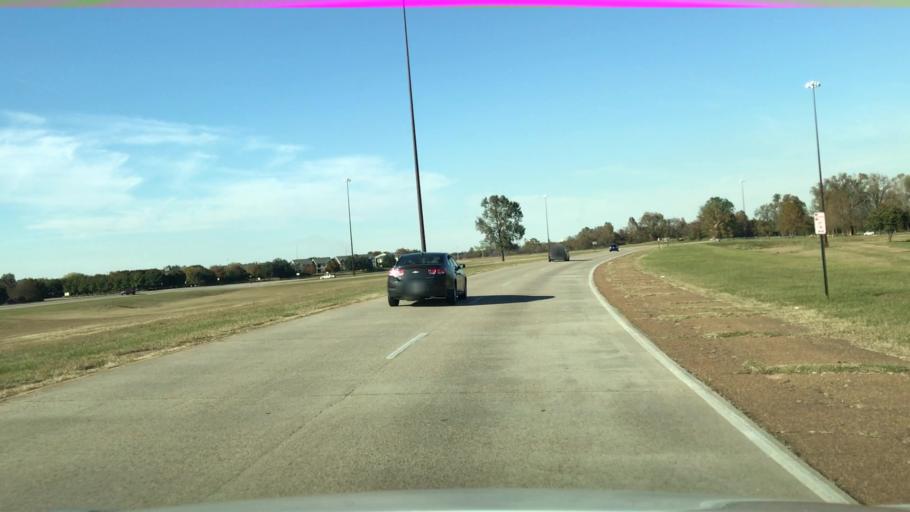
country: US
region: Louisiana
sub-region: Bossier Parish
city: Bossier City
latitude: 32.4665
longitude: -93.6854
